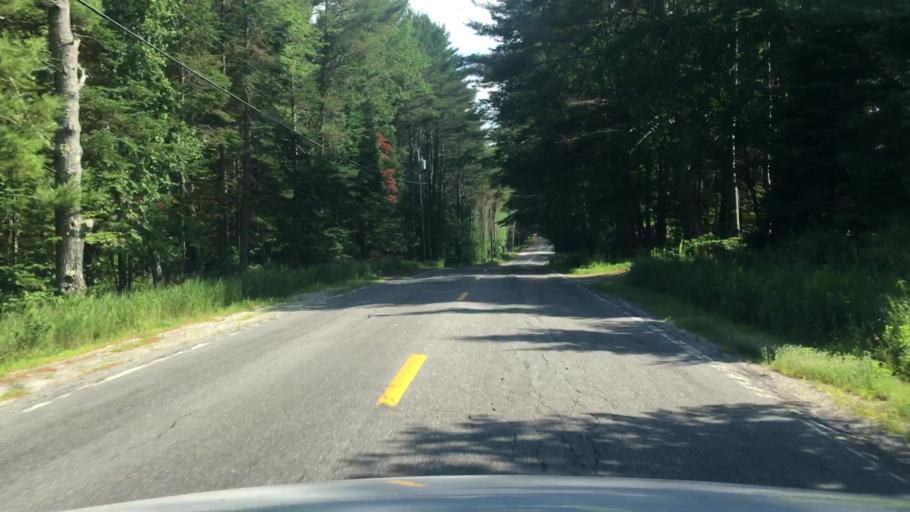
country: US
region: Maine
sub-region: Oxford County
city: Bethel
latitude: 44.3742
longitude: -70.7999
